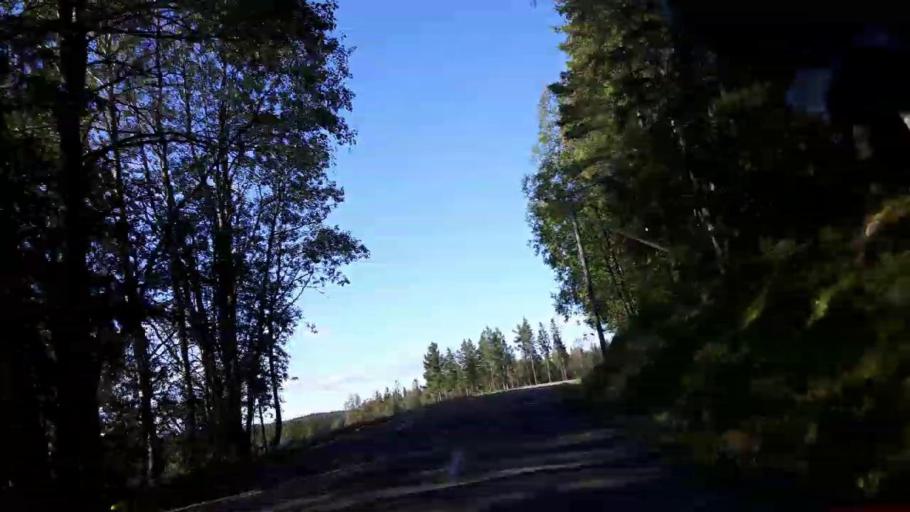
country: SE
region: Jaemtland
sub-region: Ragunda Kommun
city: Hammarstrand
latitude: 63.4999
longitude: 16.0347
